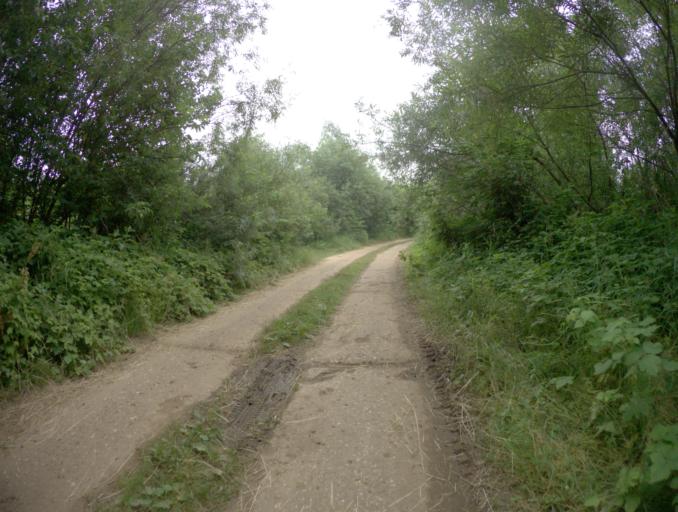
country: RU
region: Vladimir
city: Gorokhovets
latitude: 56.2107
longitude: 42.6774
